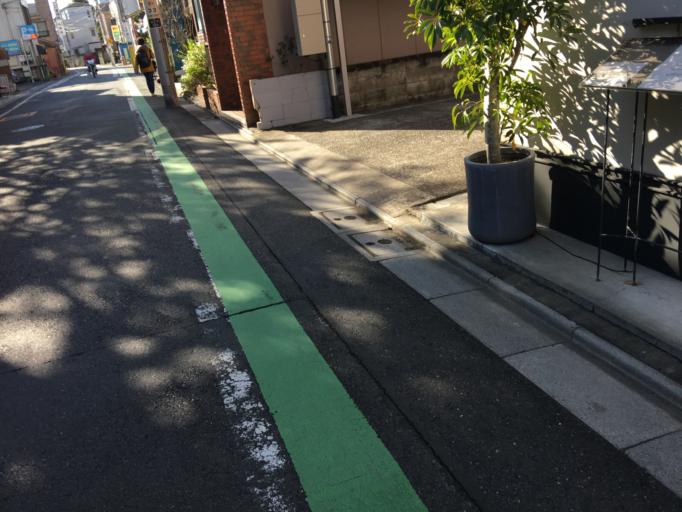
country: JP
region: Tokyo
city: Tokyo
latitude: 35.7270
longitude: 139.7684
